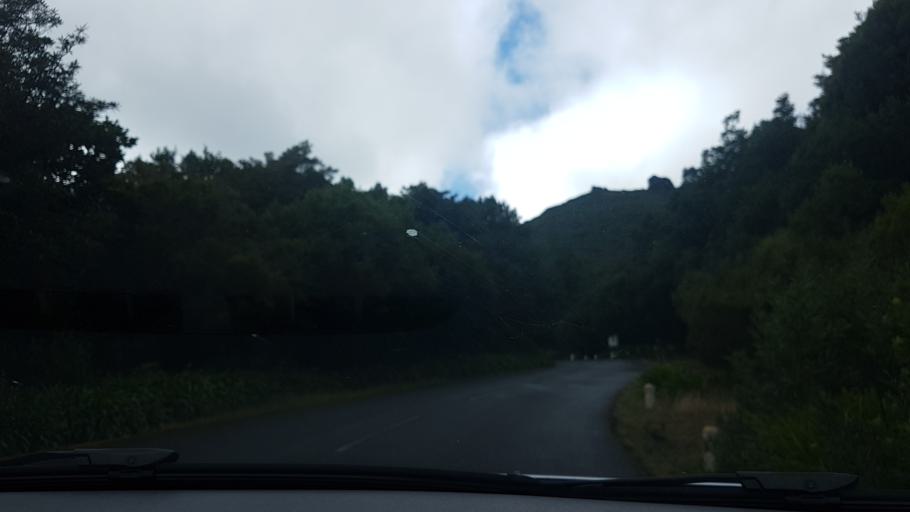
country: PT
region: Madeira
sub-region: Sao Vicente
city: Sao Vicente
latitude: 32.7581
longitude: -17.0166
